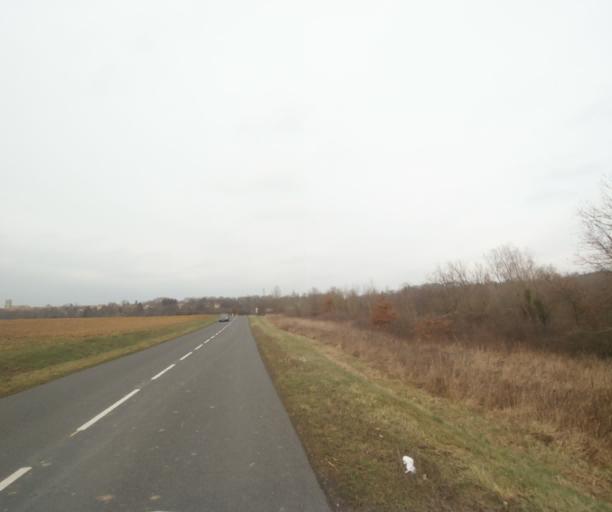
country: FR
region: Champagne-Ardenne
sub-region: Departement de la Marne
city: Pargny-sur-Saulx
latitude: 48.7434
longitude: 4.8601
